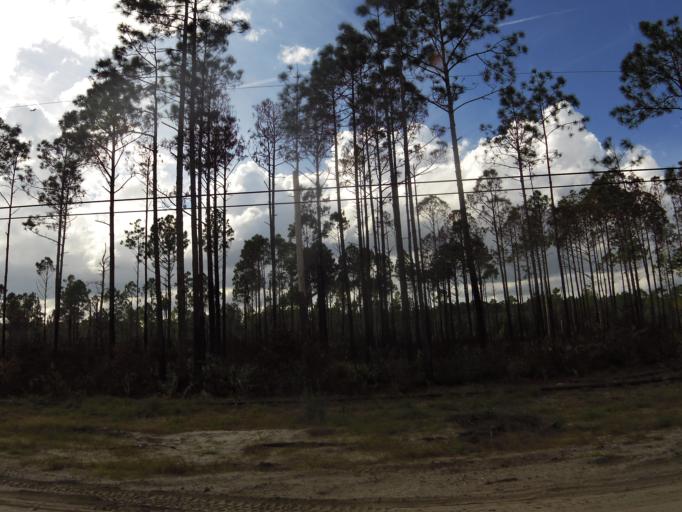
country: US
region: Florida
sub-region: Saint Johns County
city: Villano Beach
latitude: 29.9909
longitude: -81.3889
